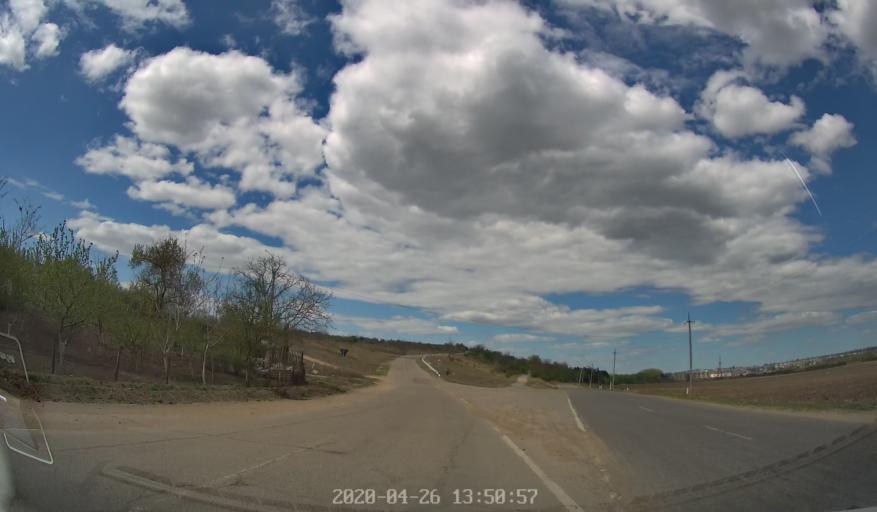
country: MD
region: Telenesti
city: Dubasari
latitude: 47.2635
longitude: 29.1280
